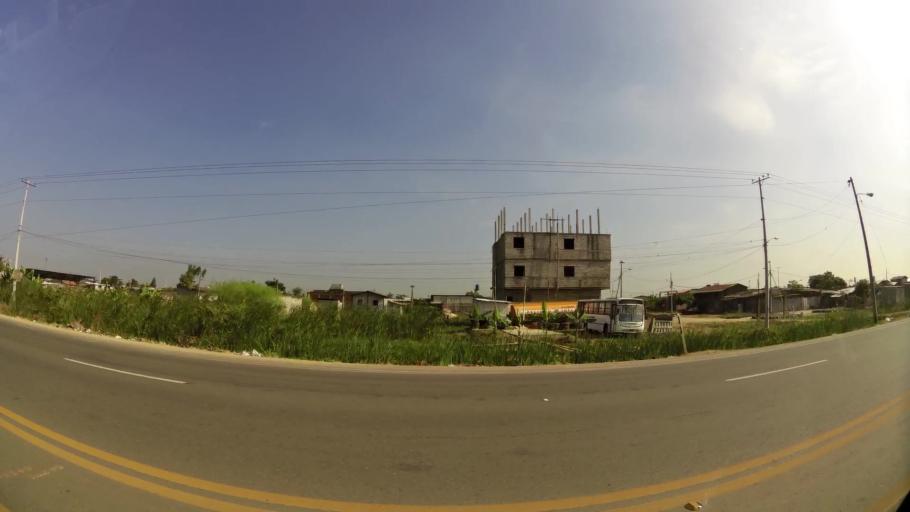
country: EC
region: Guayas
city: Eloy Alfaro
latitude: -2.1624
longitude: -79.7867
